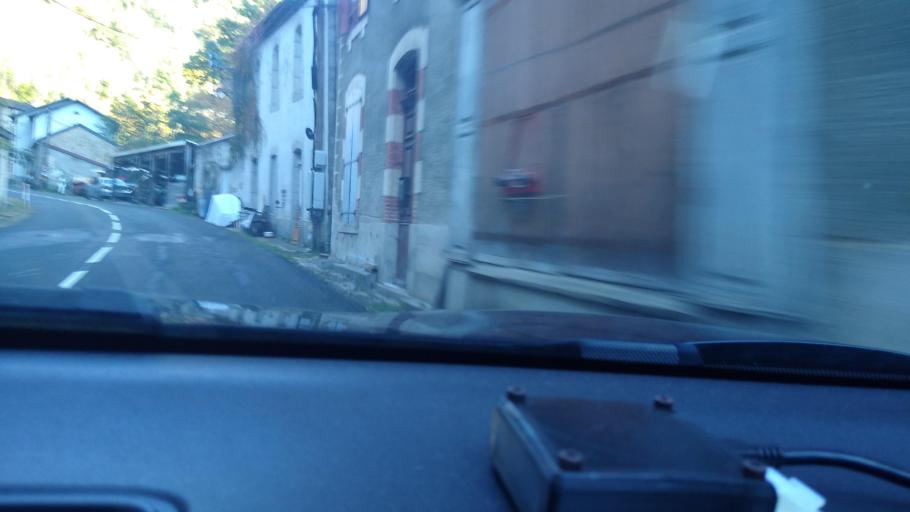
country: FR
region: Languedoc-Roussillon
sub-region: Departement de l'Aude
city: Quillan
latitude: 42.7218
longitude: 2.1195
